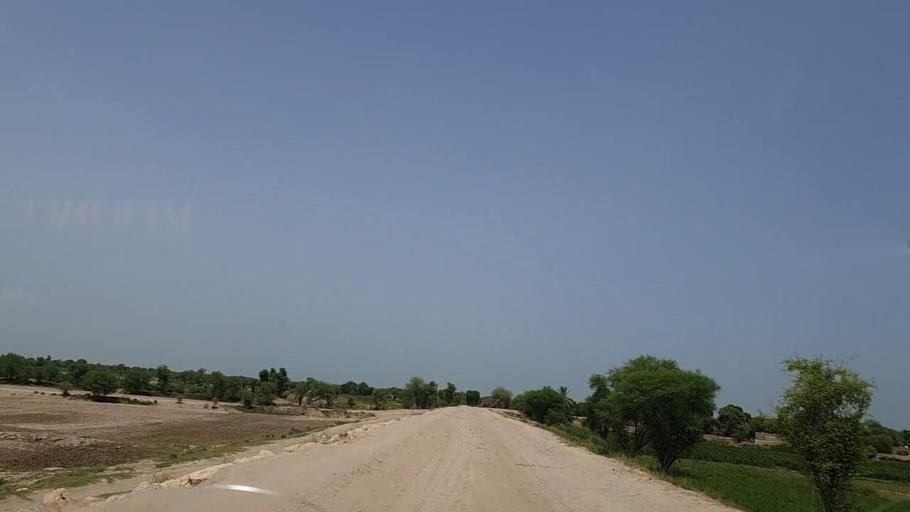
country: PK
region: Sindh
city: Tharu Shah
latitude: 27.0201
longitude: 68.1086
